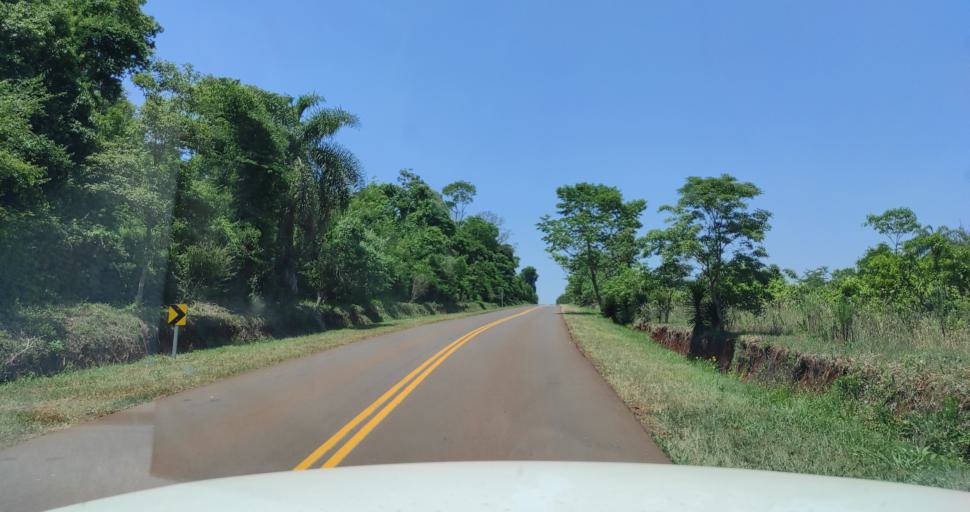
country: AR
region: Misiones
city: Capiovi
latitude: -26.9566
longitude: -55.0918
